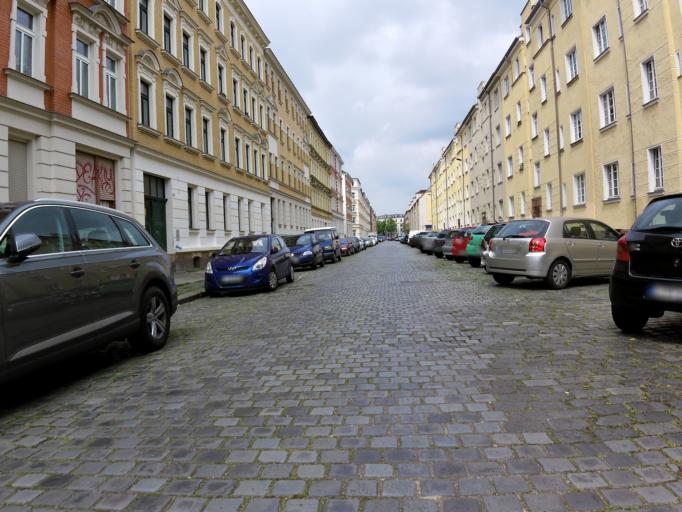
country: DE
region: Saxony
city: Leipzig
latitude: 51.3074
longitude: 12.3815
